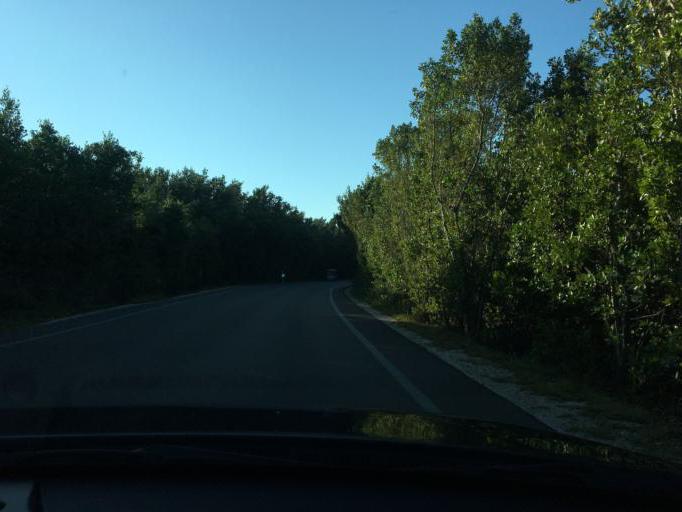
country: US
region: Florida
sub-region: Lee County
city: Pine Island Center
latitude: 26.5374
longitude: -82.1943
